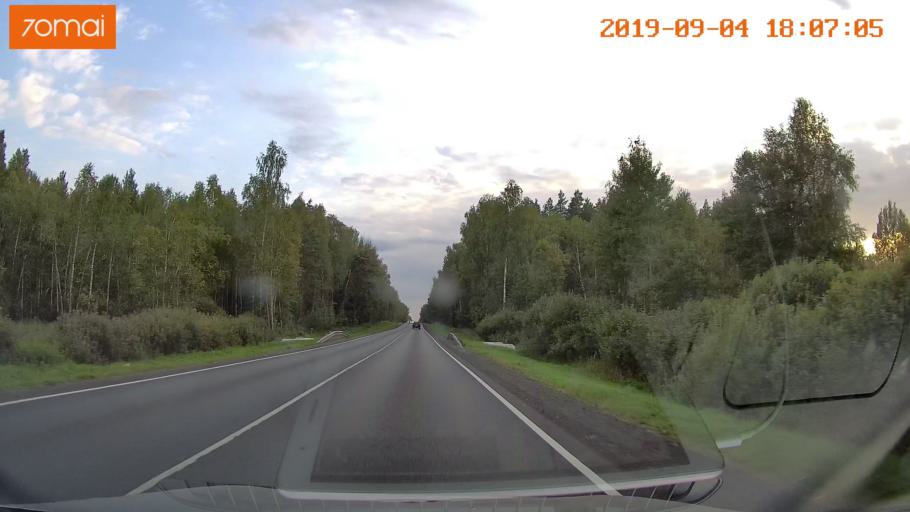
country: RU
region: Moskovskaya
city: Khorlovo
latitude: 55.4236
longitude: 38.8060
